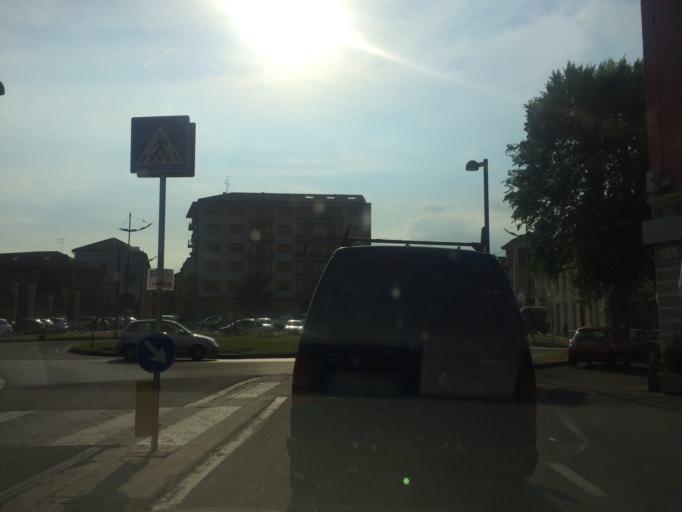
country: IT
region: Piedmont
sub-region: Provincia di Cuneo
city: Alba
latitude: 44.7006
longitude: 8.0405
